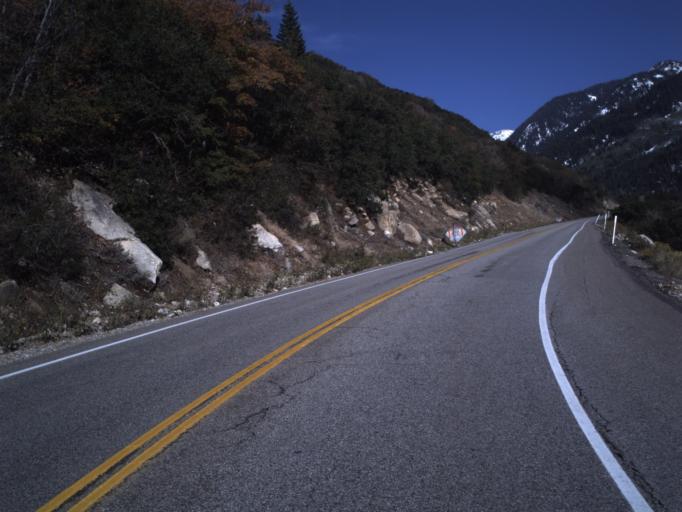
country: US
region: Utah
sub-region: Salt Lake County
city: Granite
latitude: 40.5727
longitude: -111.7261
